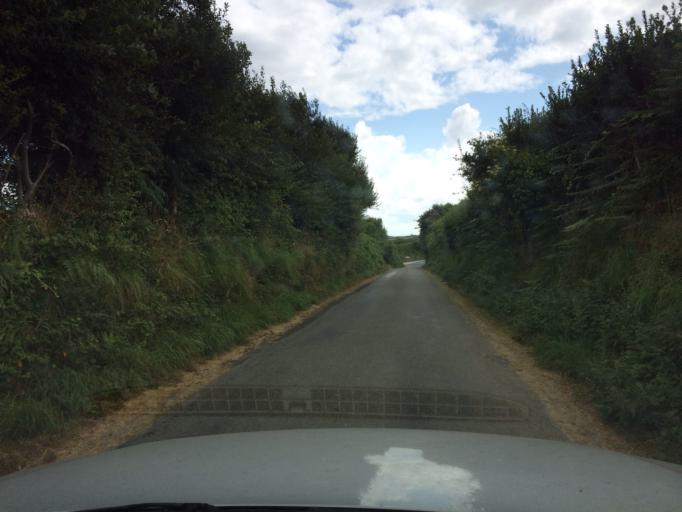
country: FR
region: Lower Normandy
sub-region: Departement de la Manche
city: Beaumont-Hague
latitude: 49.6829
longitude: -1.8591
